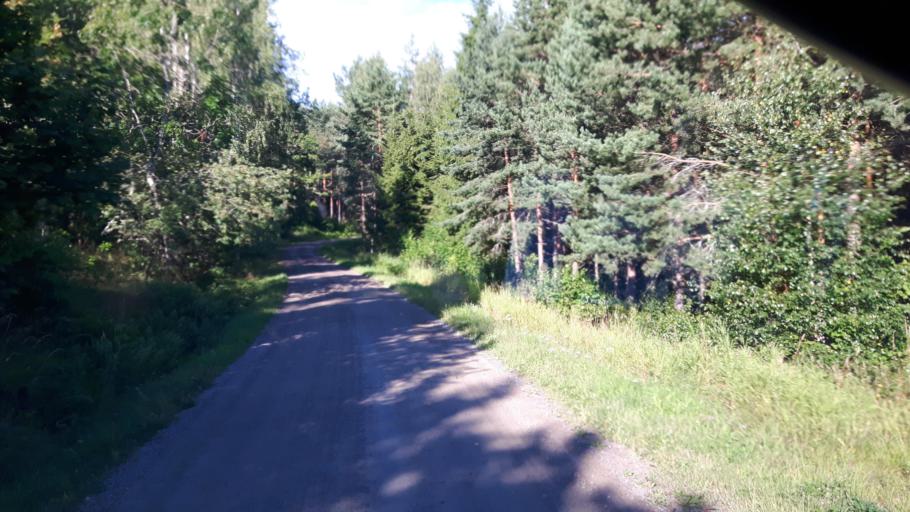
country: SE
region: OEstergoetland
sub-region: Kinda Kommun
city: Kisa
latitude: 58.0636
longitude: 15.6094
